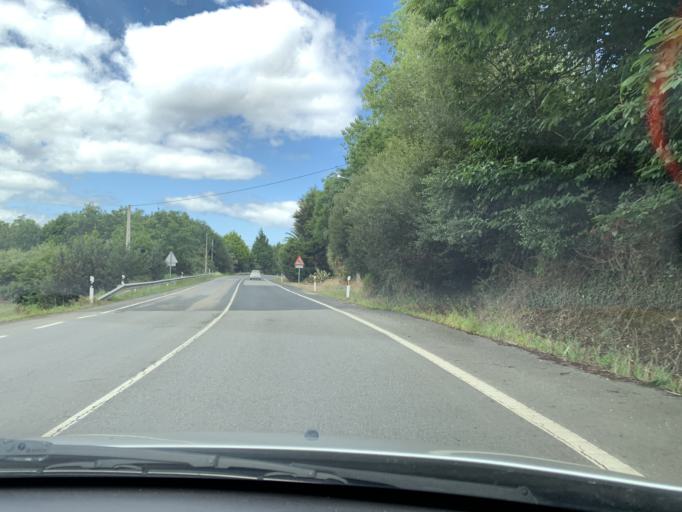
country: ES
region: Galicia
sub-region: Provincia de Lugo
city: Barreiros
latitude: 43.5261
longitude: -7.2664
